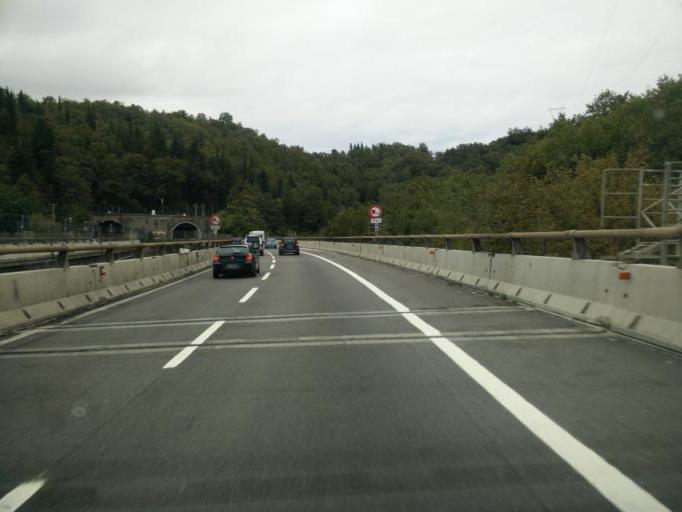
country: IT
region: Tuscany
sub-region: Province of Florence
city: Cavallina
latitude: 43.9397
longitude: 11.2218
